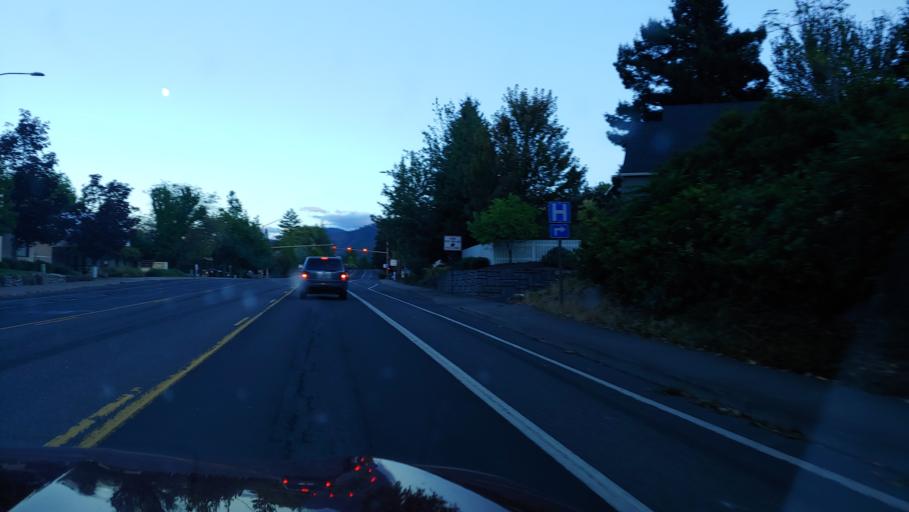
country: US
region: Oregon
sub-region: Jackson County
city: Ashland
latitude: 42.2079
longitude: -122.7226
